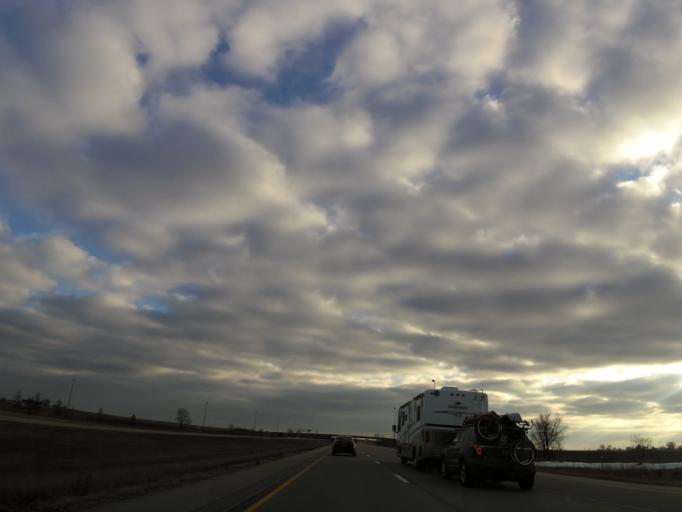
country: US
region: Illinois
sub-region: LaSalle County
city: Earlville
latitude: 41.7228
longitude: -89.0096
